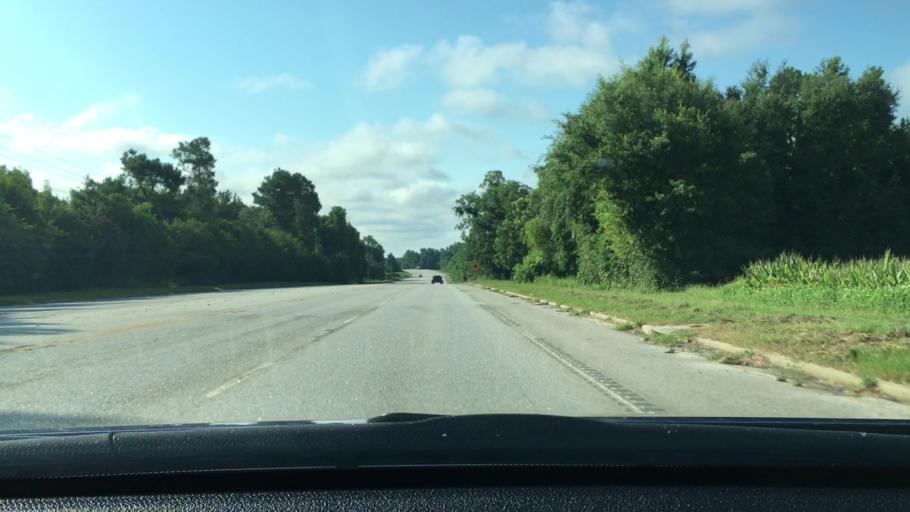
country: US
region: South Carolina
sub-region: Clarendon County
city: Manning
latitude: 33.7551
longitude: -80.2244
